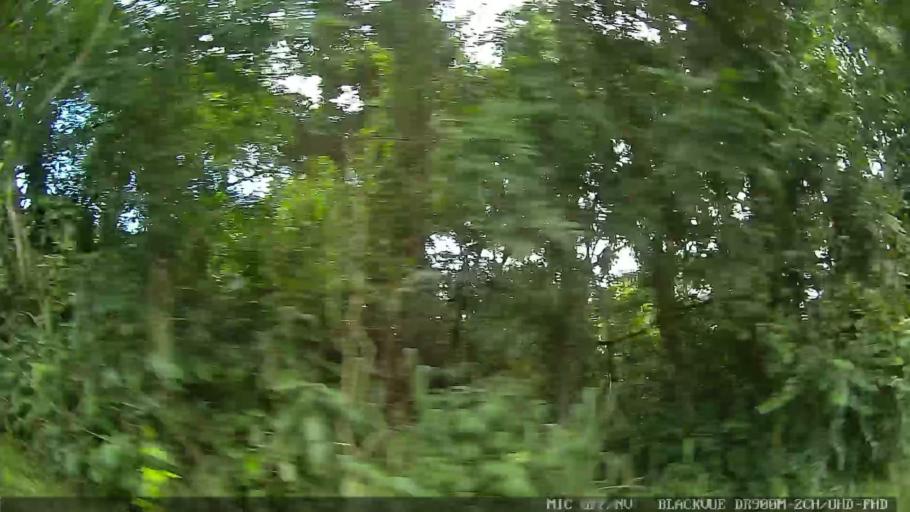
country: BR
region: Sao Paulo
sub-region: Iguape
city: Iguape
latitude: -24.6654
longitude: -47.4336
